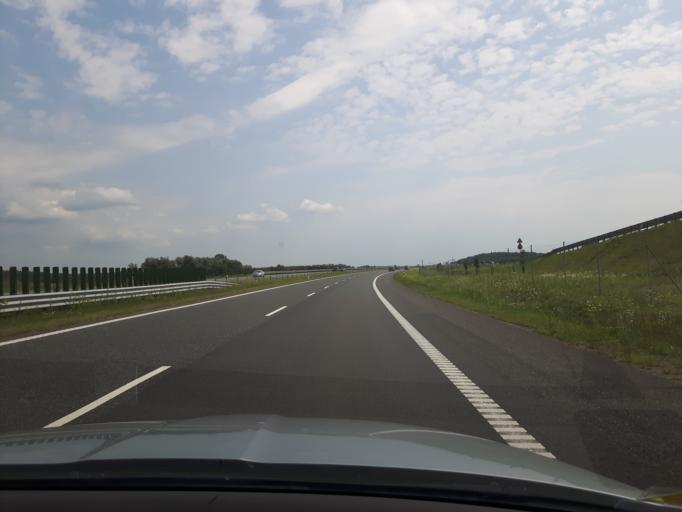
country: PL
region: Warmian-Masurian Voivodeship
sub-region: Powiat nidzicki
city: Nidzica
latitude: 53.3988
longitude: 20.3569
